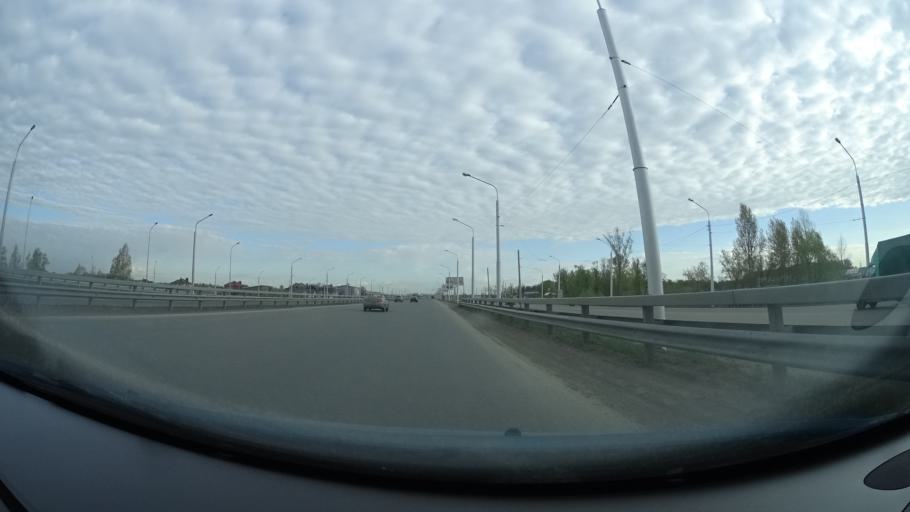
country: RU
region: Bashkortostan
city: Ufa
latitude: 54.7655
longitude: 55.9558
